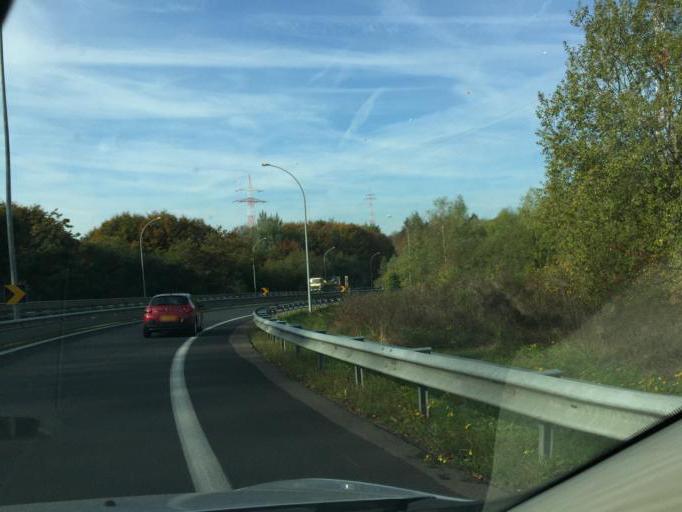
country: LU
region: Luxembourg
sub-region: Canton de Luxembourg
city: Sandweiler
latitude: 49.6391
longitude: 6.1908
